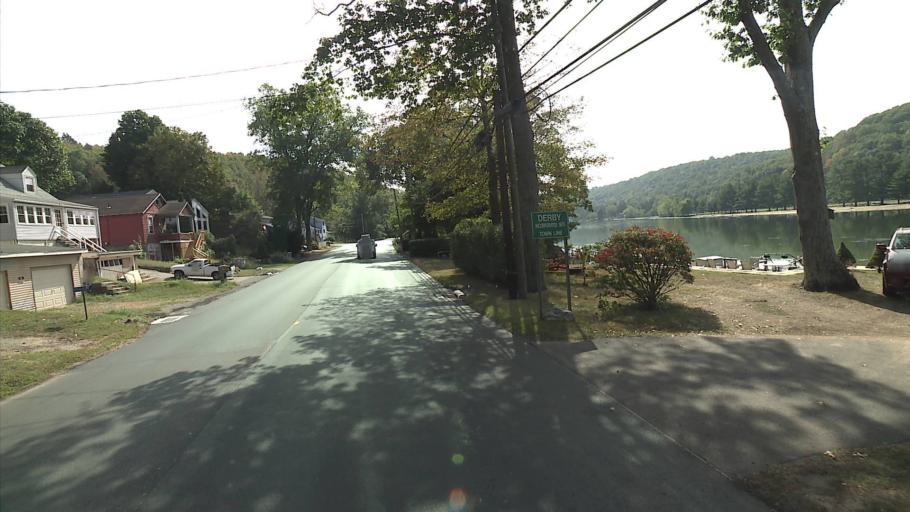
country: US
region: Connecticut
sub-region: Fairfield County
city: Shelton
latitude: 41.3459
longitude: -73.1237
